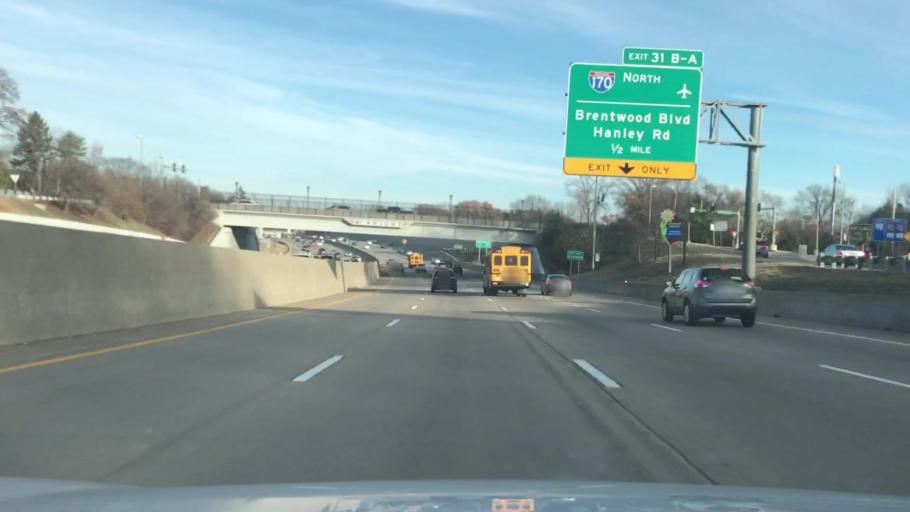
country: US
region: Missouri
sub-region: Saint Louis County
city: Brentwood
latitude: 38.6298
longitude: -90.3638
